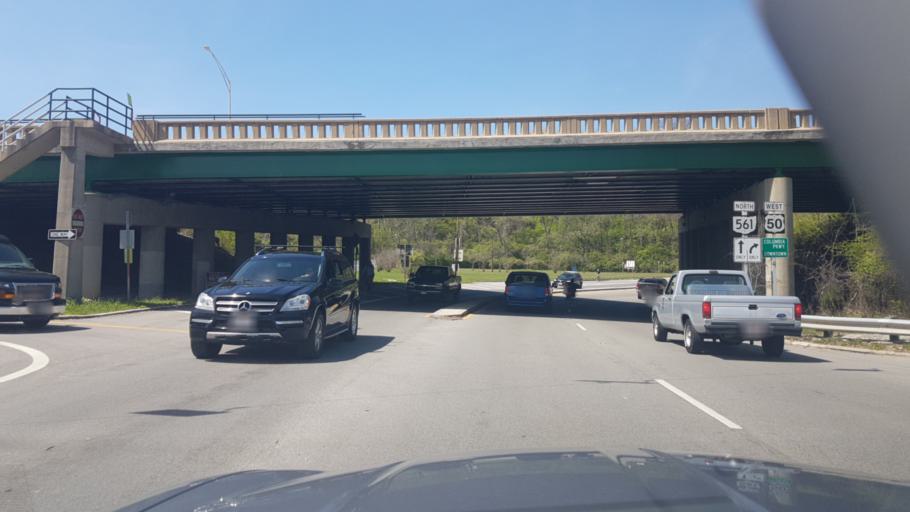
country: US
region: Ohio
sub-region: Hamilton County
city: Fairfax
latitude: 39.1206
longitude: -84.4179
